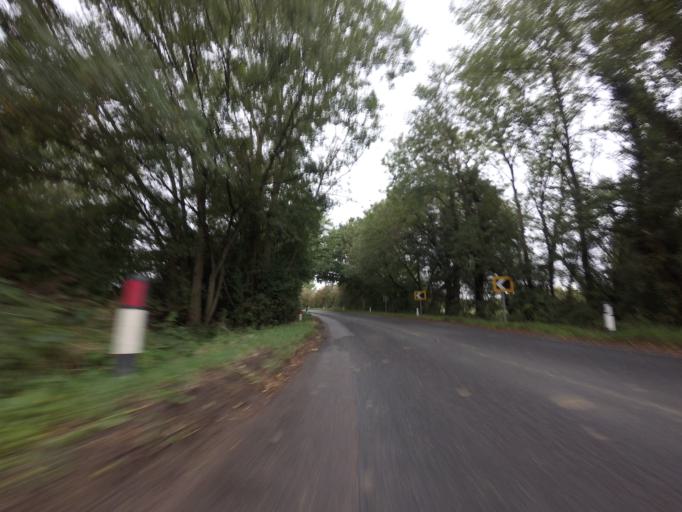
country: GB
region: England
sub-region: Cambridgeshire
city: Wimpole
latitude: 52.1845
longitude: -0.0454
